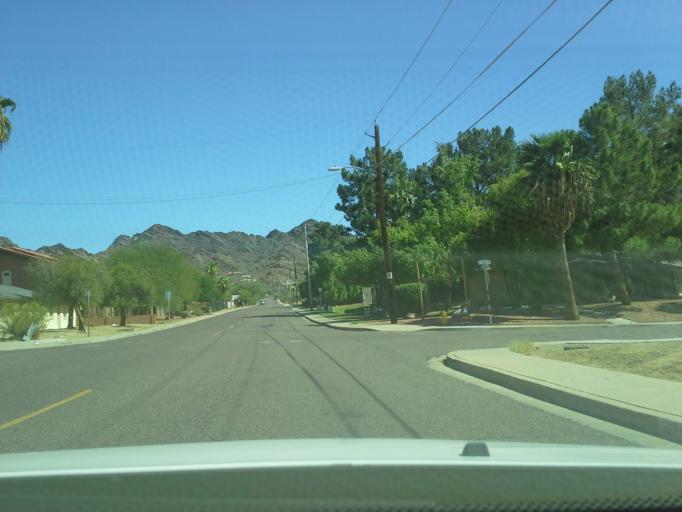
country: US
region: Arizona
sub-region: Maricopa County
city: Paradise Valley
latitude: 33.5749
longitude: -112.0547
